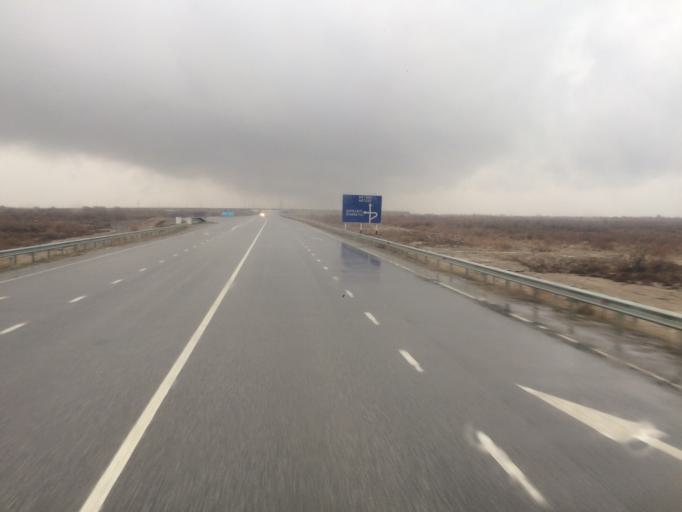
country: KZ
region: Qyzylorda
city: Terenozek
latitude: 44.8823
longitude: 65.1382
